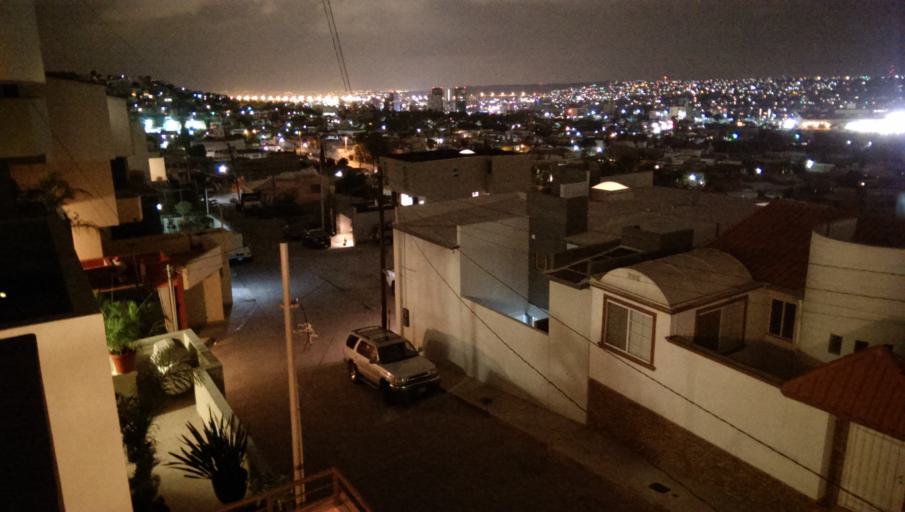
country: MX
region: Baja California
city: Tijuana
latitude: 32.4969
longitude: -116.9971
